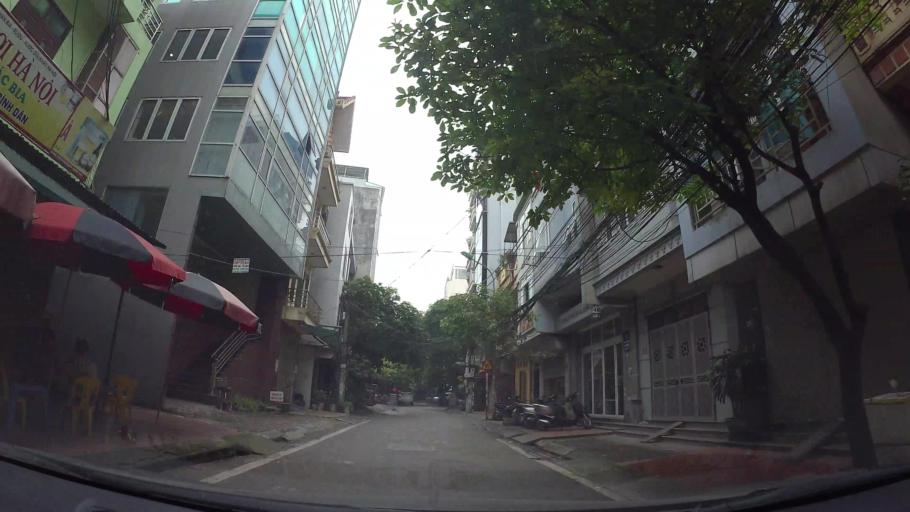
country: VN
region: Ha Noi
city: Van Dien
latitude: 20.9672
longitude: 105.8444
